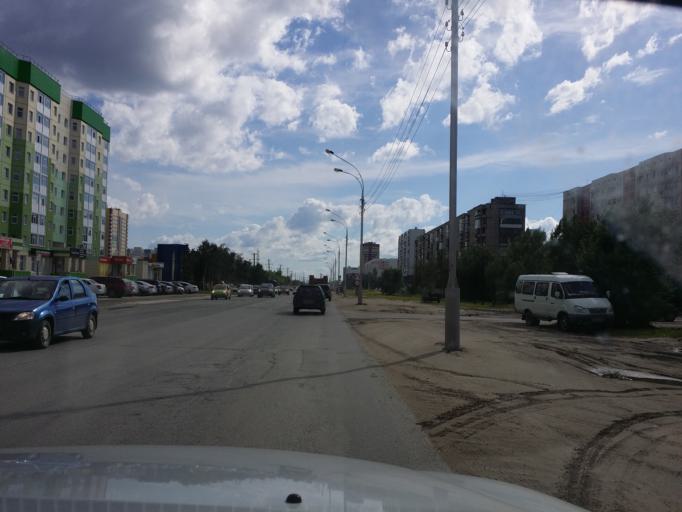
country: RU
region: Khanty-Mansiyskiy Avtonomnyy Okrug
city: Nizhnevartovsk
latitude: 60.9334
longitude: 76.6113
